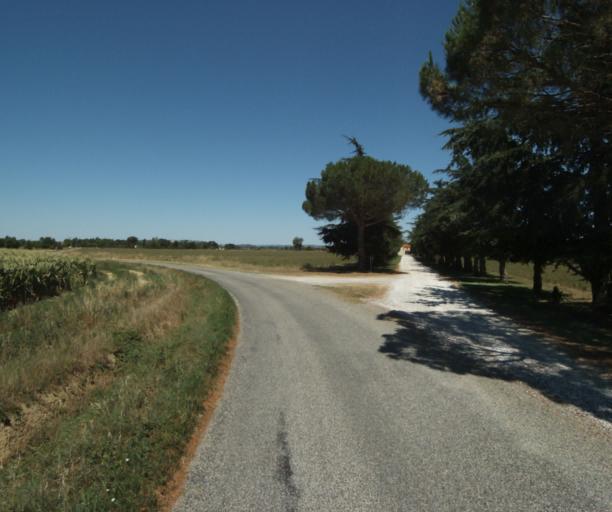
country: FR
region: Midi-Pyrenees
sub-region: Departement de la Haute-Garonne
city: Revel
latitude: 43.4482
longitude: 1.9503
